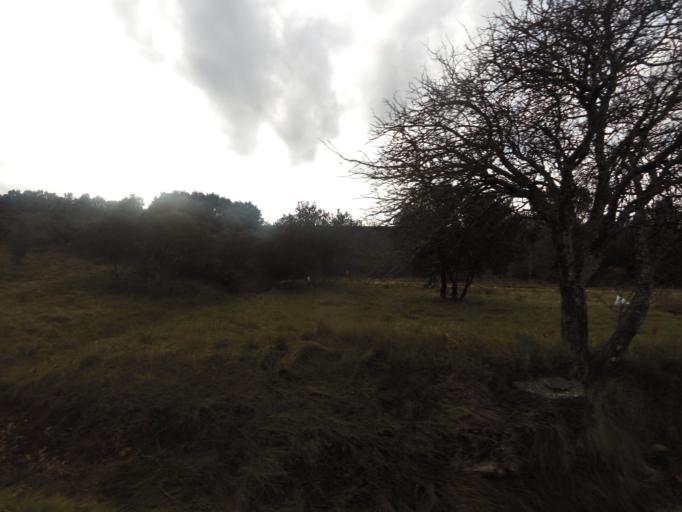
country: FR
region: Languedoc-Roussillon
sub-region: Departement du Gard
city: La Calmette
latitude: 43.8832
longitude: 4.2529
